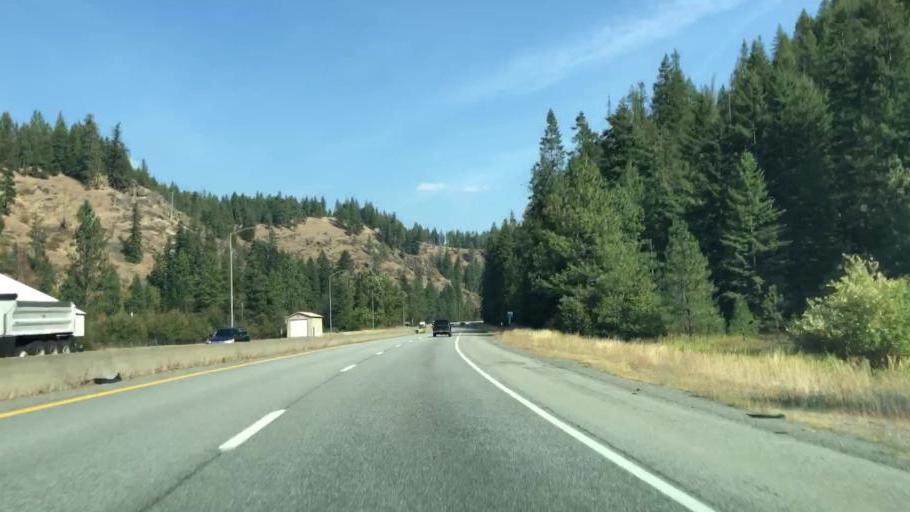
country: US
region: Idaho
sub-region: Kootenai County
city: Coeur d'Alene
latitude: 47.6306
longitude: -116.6106
